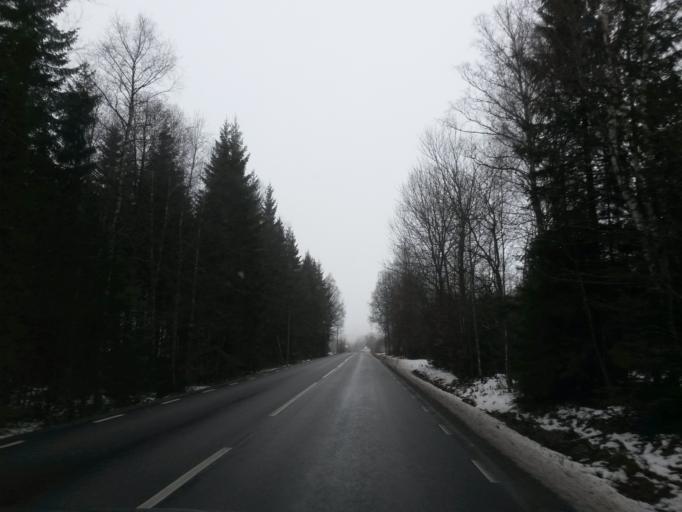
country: SE
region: Vaestra Goetaland
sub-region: Ulricehamns Kommun
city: Ulricehamn
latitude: 57.6652
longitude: 13.4108
